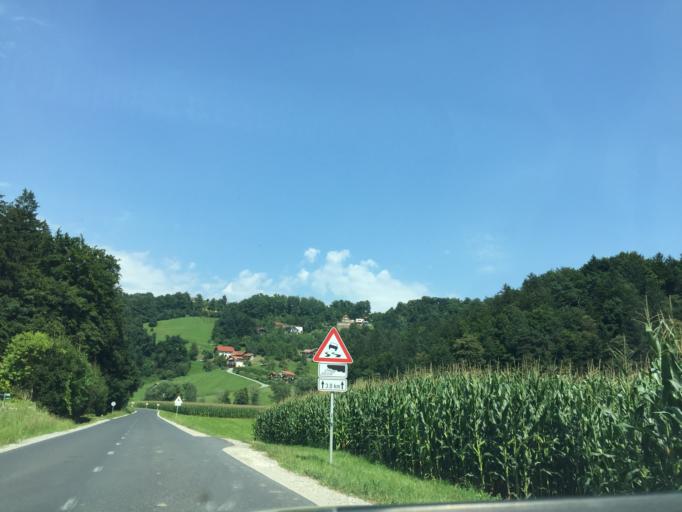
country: SI
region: Polzela
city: Polzela
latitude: 46.2887
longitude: 15.0857
